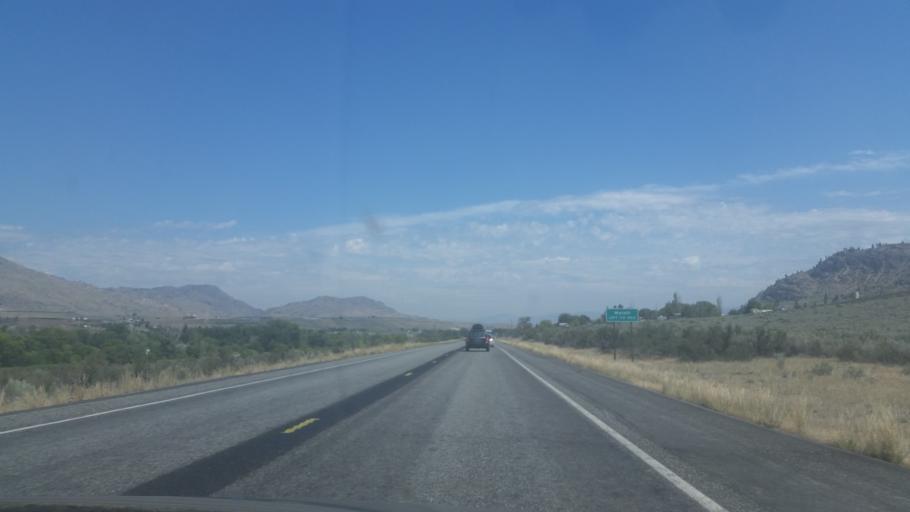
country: US
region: Washington
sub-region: Okanogan County
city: Okanogan
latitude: 48.2735
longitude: -119.7111
